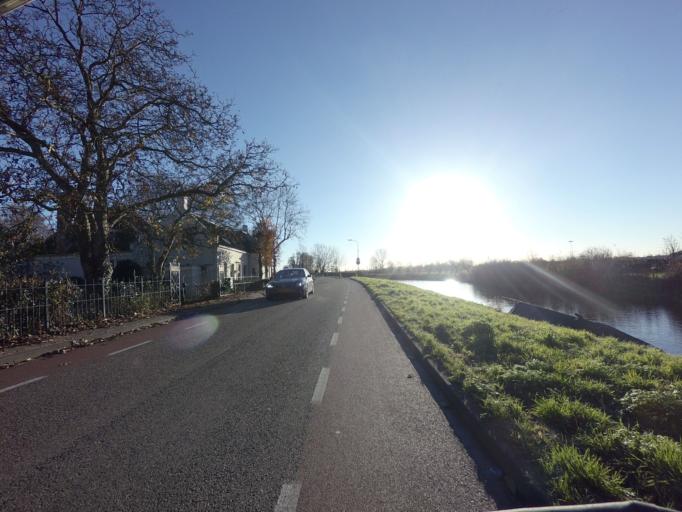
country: NL
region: Utrecht
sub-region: Stichtse Vecht
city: Vreeland
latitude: 52.2287
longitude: 4.9982
